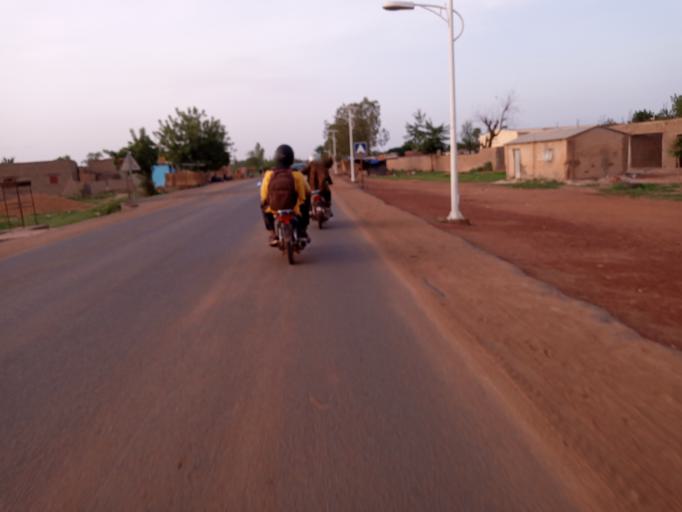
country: ML
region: Bamako
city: Bamako
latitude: 12.3077
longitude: -8.1546
